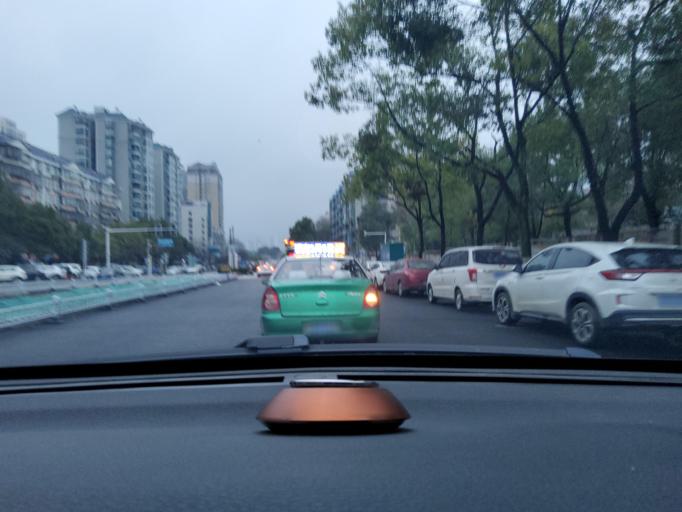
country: CN
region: Hubei
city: Tuanchengshan
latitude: 30.1931
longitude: 115.0266
